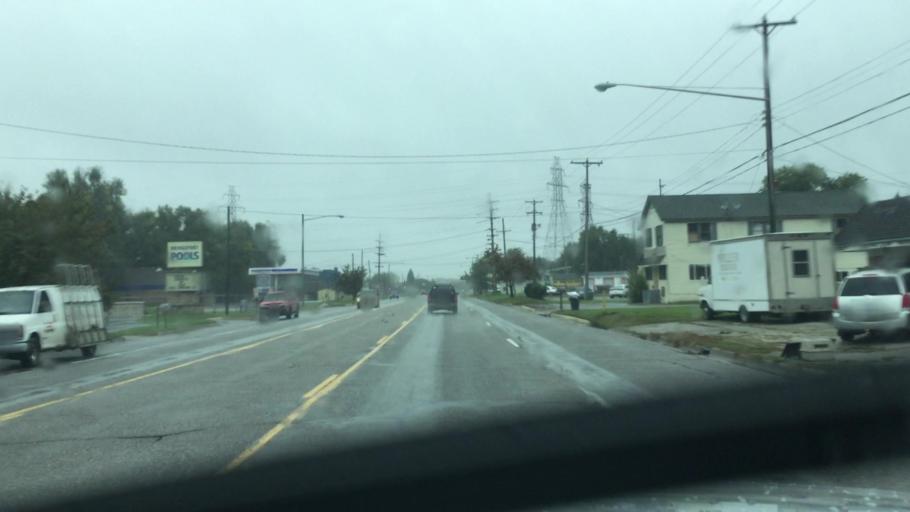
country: US
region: Michigan
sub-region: Saginaw County
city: Buena Vista
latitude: 43.3897
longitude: -83.9045
